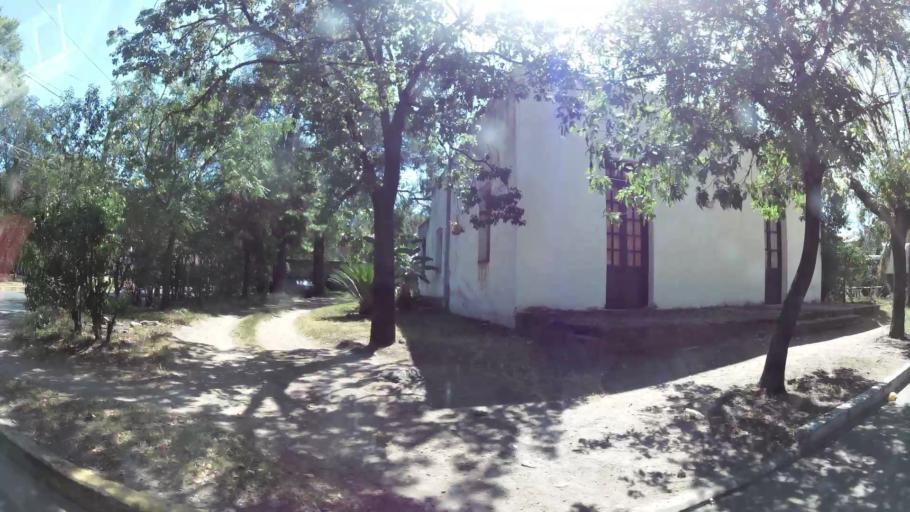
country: AR
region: Cordoba
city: Saldan
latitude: -31.2996
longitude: -64.3018
